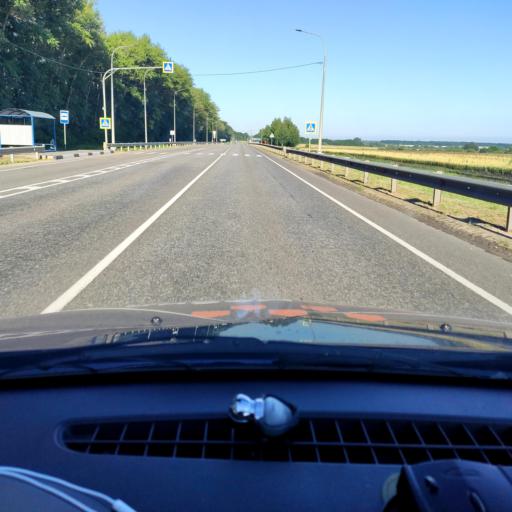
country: RU
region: Orjol
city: Pokrovskoye
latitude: 52.6203
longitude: 36.7591
